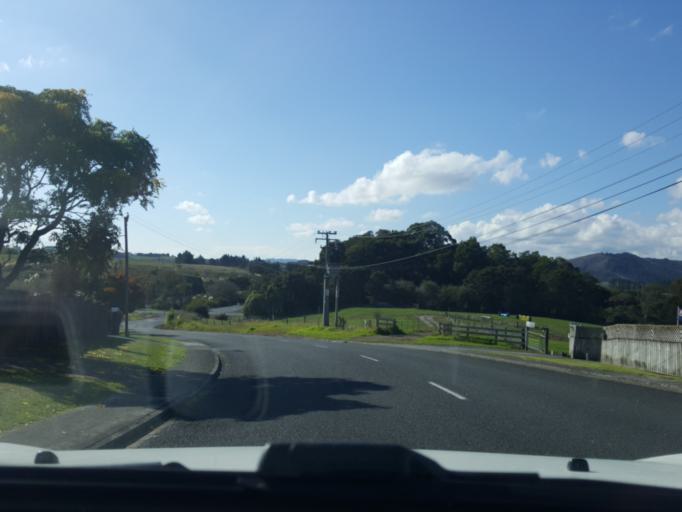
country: NZ
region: Waikato
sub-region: Waikato District
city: Ngaruawahia
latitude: -37.5416
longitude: 175.1734
